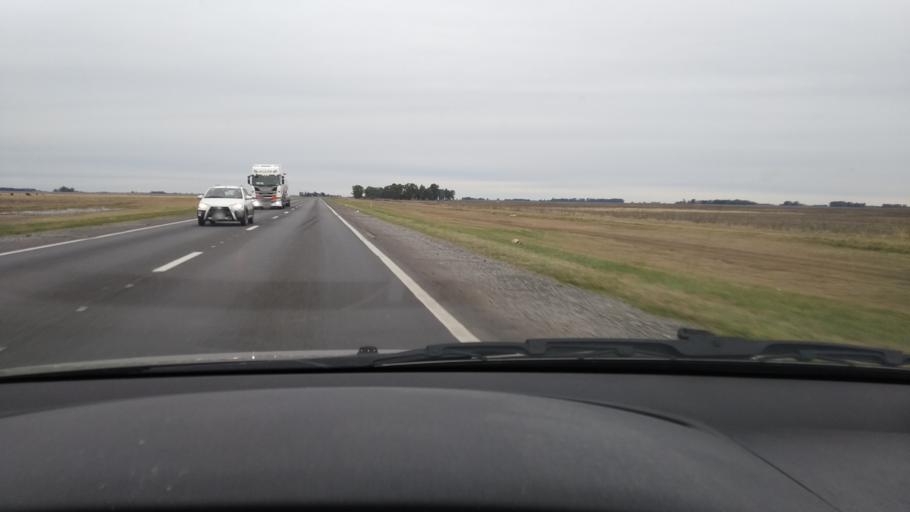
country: AR
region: Buenos Aires
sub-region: Partido de Las Flores
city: Las Flores
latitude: -36.1844
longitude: -59.2562
